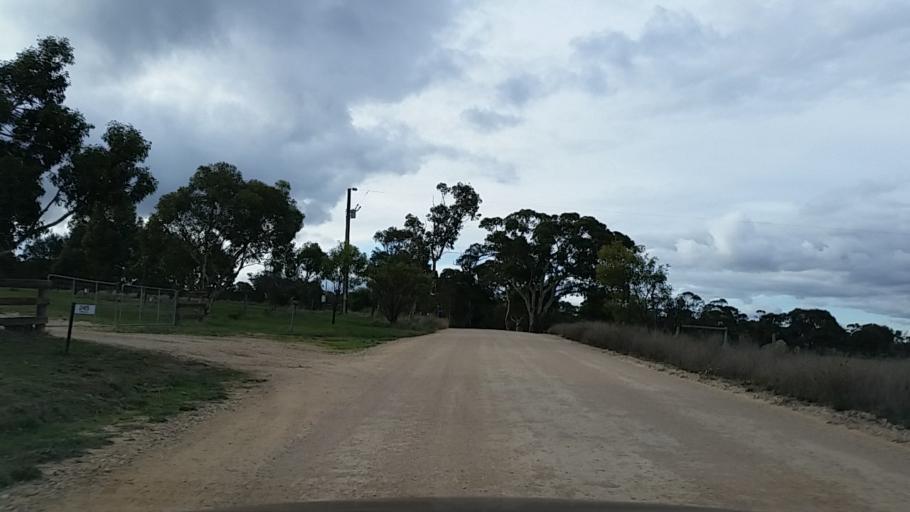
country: AU
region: South Australia
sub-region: Mount Barker
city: Callington
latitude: -34.9882
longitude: 139.0574
